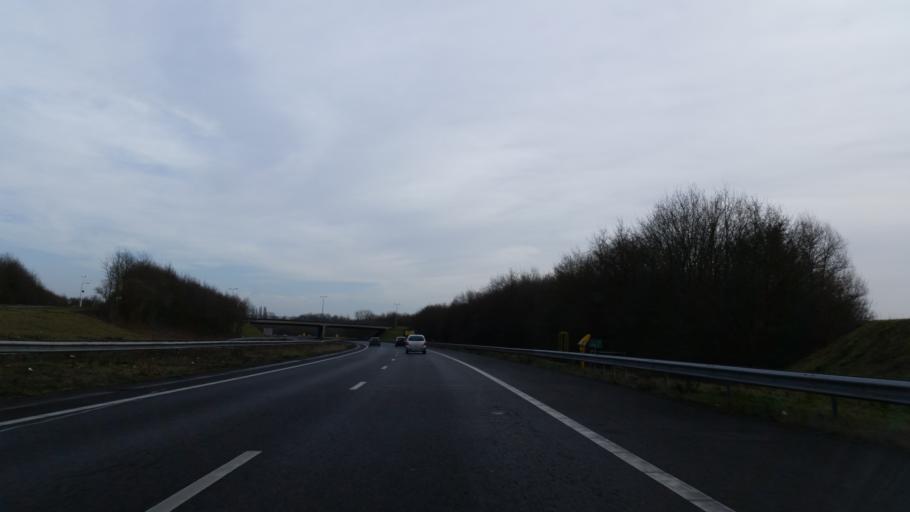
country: NL
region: Limburg
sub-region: Gemeente Weert
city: Weert
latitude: 51.2775
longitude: 5.6602
